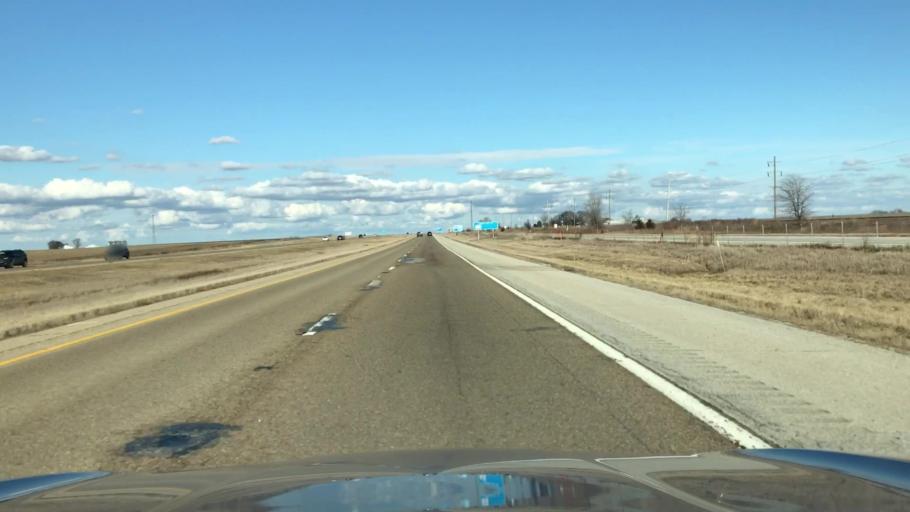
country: US
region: Illinois
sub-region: McLean County
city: Chenoa
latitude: 40.7124
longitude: -88.7418
